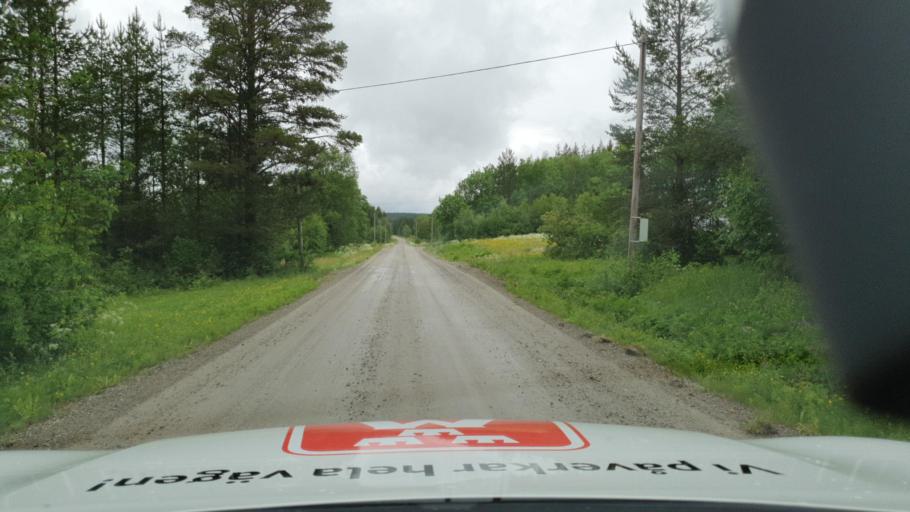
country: SE
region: Vaesterbotten
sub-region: Dorotea Kommun
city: Dorotea
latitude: 64.0181
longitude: 16.7938
